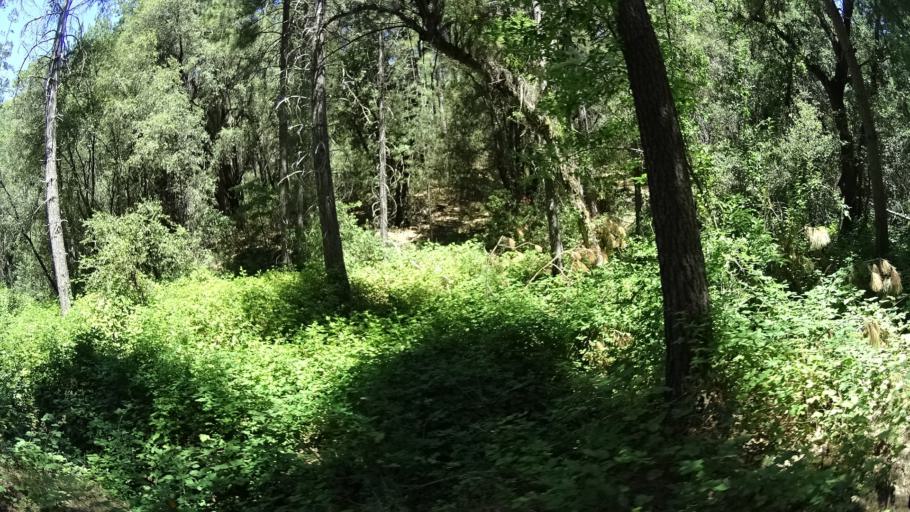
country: US
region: California
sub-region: Calaveras County
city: Forest Meadows
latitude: 38.1388
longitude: -120.4230
